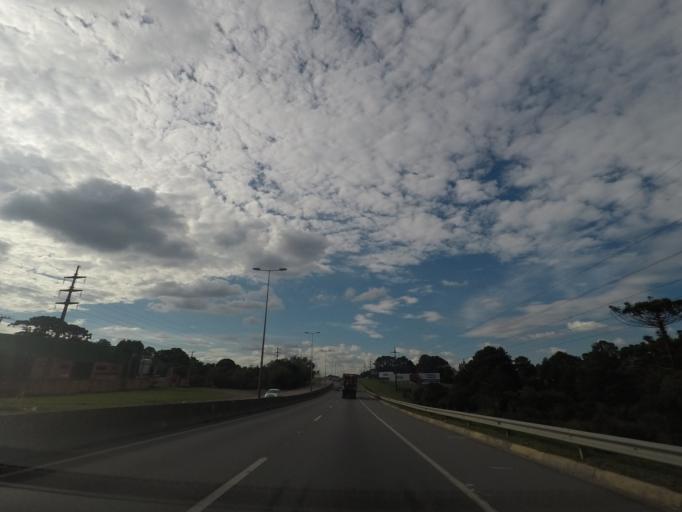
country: BR
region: Parana
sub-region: Araucaria
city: Araucaria
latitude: -25.5896
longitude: -49.3150
